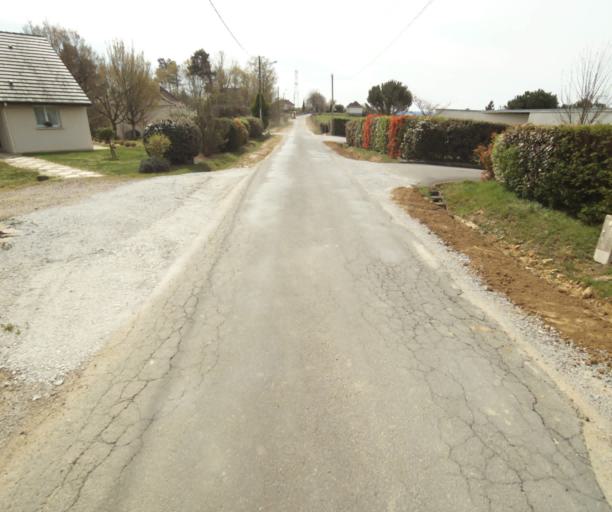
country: FR
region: Limousin
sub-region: Departement de la Correze
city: Naves
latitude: 45.2989
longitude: 1.7801
